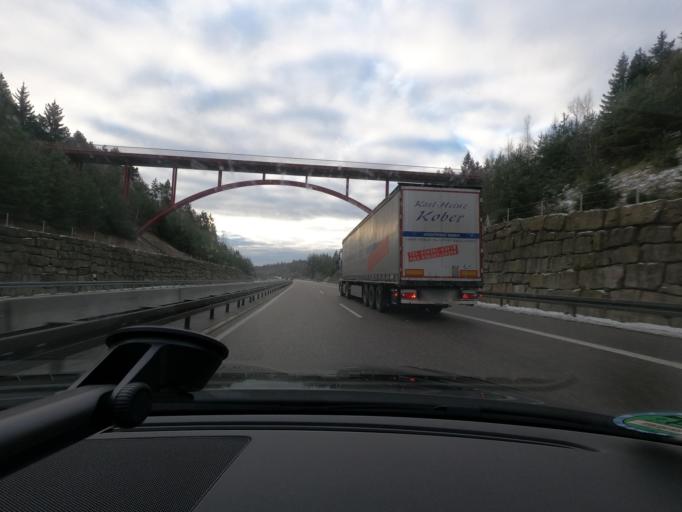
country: DE
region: Thuringia
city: Sankt Kilian
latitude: 50.5358
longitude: 10.7415
